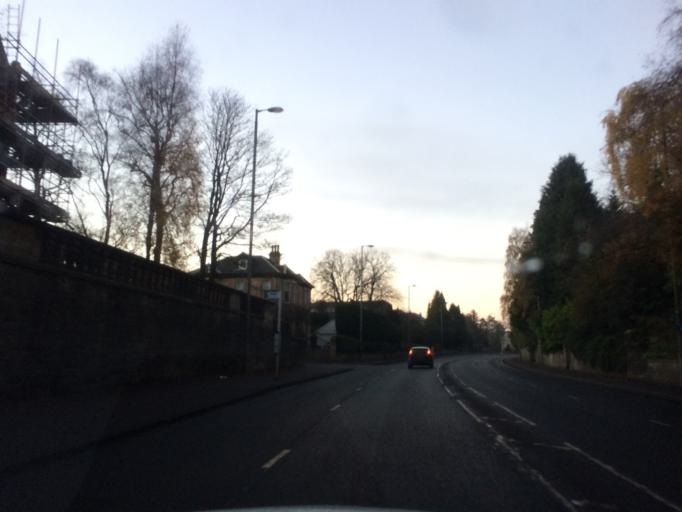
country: GB
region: Scotland
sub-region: East Renfrewshire
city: Giffnock
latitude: 55.7983
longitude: -4.2967
